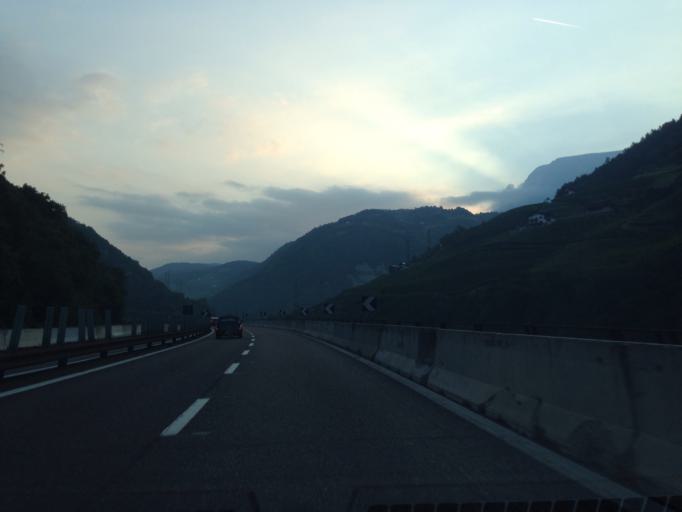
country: IT
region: Trentino-Alto Adige
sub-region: Bolzano
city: Collalbo
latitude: 46.5076
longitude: 11.4647
